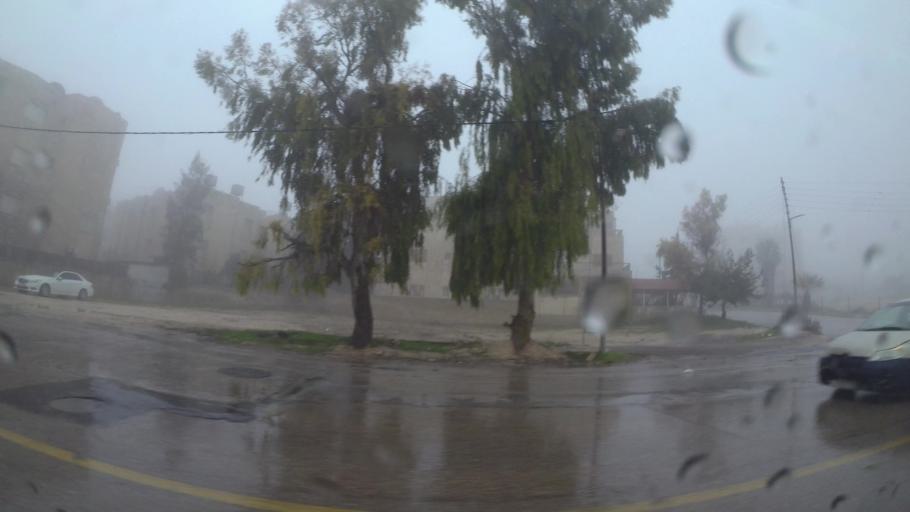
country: JO
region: Amman
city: Al Jubayhah
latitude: 32.0098
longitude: 35.8823
